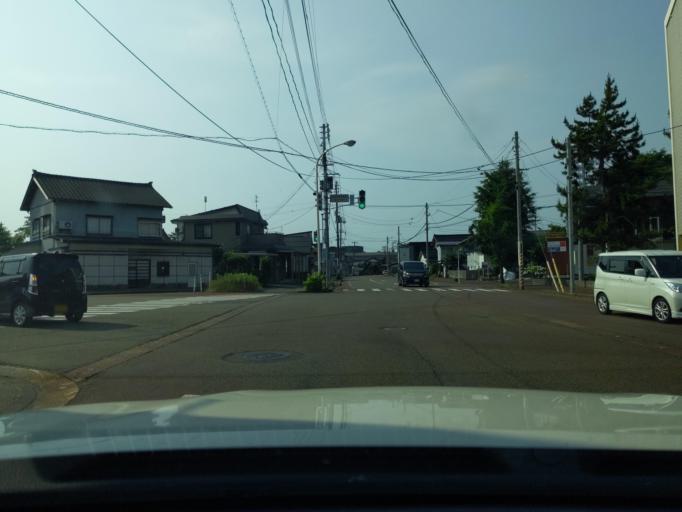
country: JP
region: Niigata
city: Nagaoka
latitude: 37.4371
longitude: 138.8562
